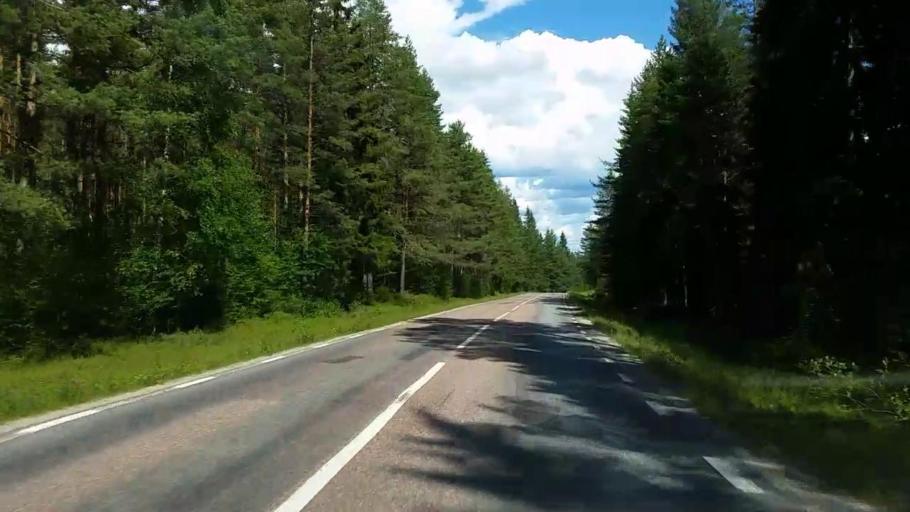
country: SE
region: Gaevleborg
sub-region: Ovanakers Kommun
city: Edsbyn
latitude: 61.3301
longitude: 15.5260
